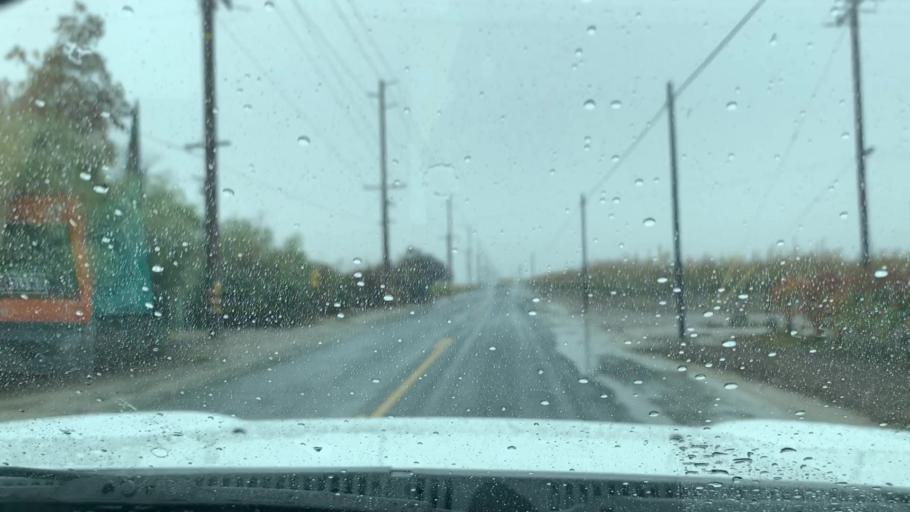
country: US
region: California
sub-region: Kern County
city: Delano
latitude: 35.8340
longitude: -119.2233
